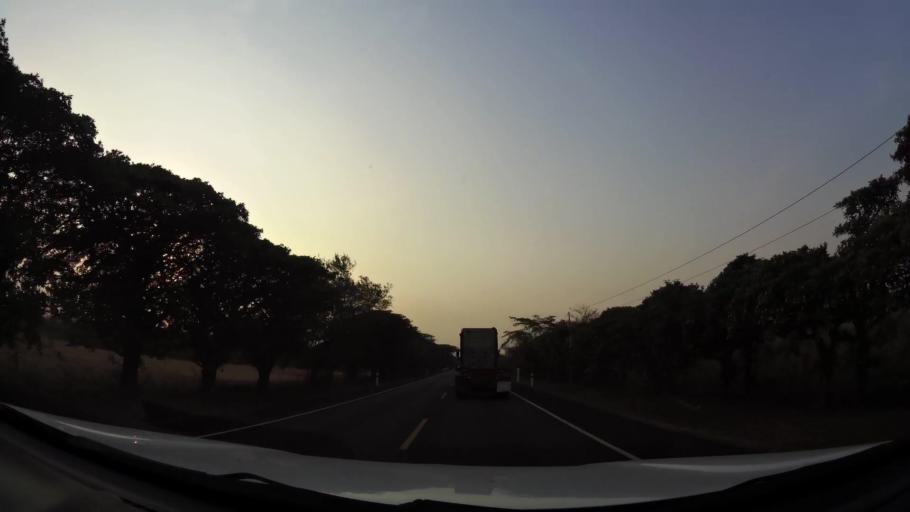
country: NI
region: Leon
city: Nagarote
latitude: 12.2887
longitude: -86.5863
